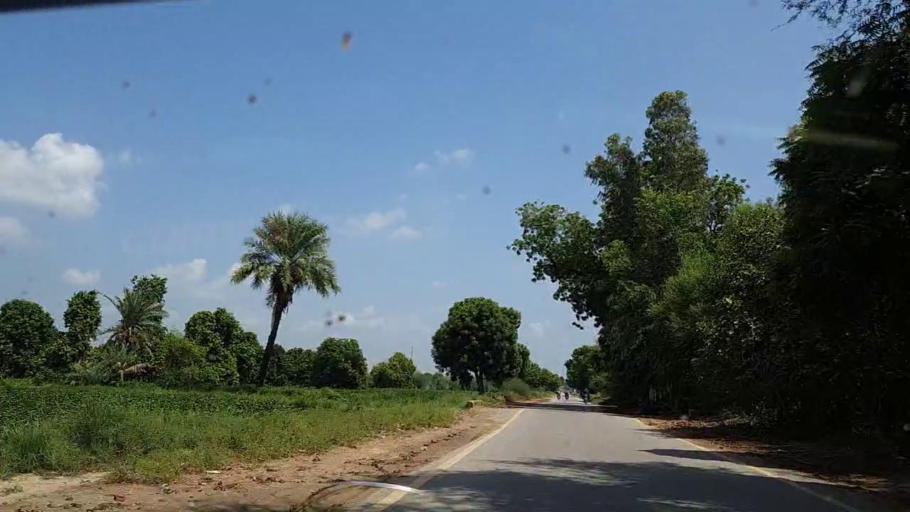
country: PK
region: Sindh
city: Tharu Shah
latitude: 26.9498
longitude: 68.1093
